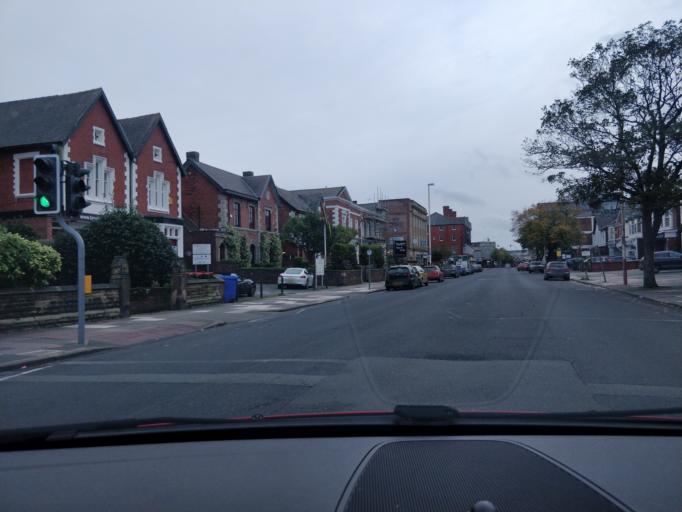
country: GB
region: England
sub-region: Sefton
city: Southport
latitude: 53.6490
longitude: -3.0003
